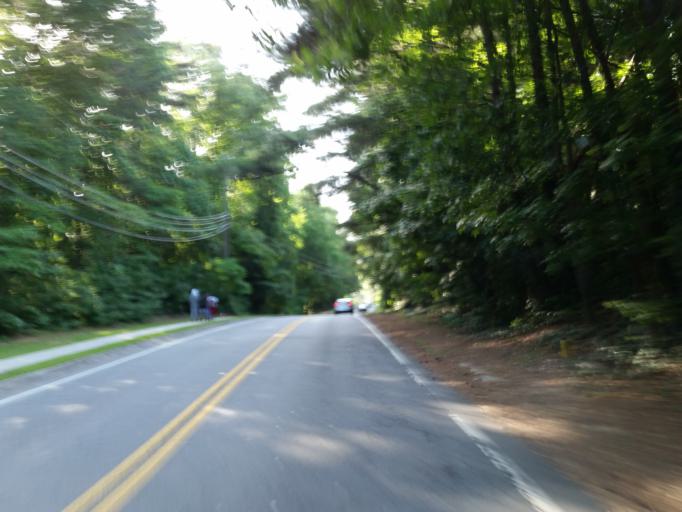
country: US
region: Georgia
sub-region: Cobb County
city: Vinings
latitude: 33.9147
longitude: -84.4725
